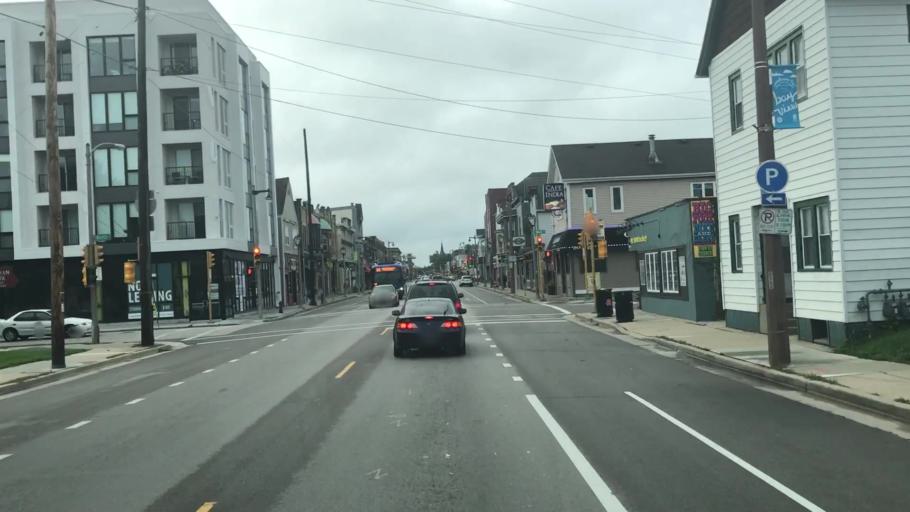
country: US
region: Wisconsin
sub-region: Milwaukee County
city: Milwaukee
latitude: 43.0049
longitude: -87.9058
